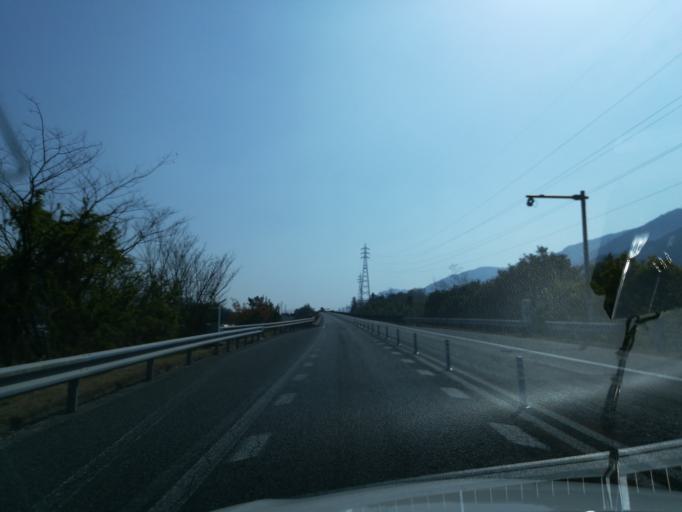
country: JP
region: Tokushima
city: Ikedacho
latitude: 34.0355
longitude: 133.8757
